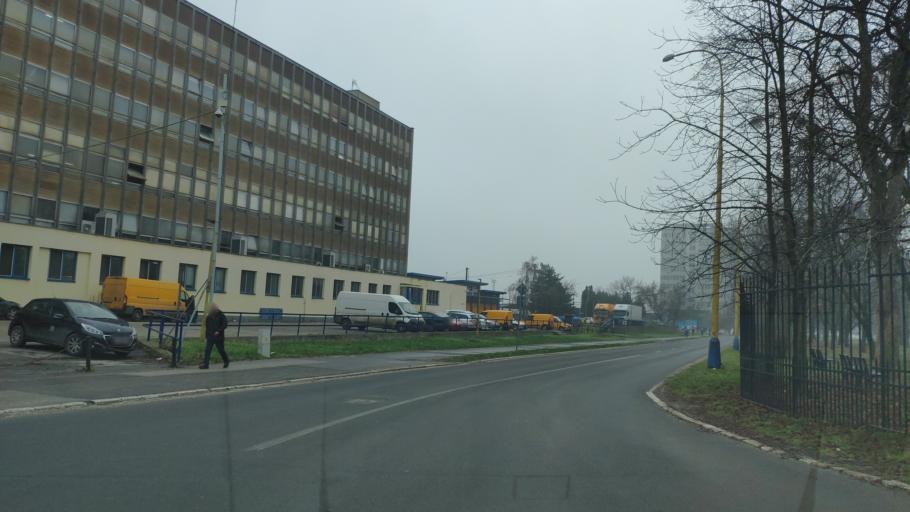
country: SK
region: Kosicky
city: Kosice
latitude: 48.7258
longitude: 21.2659
